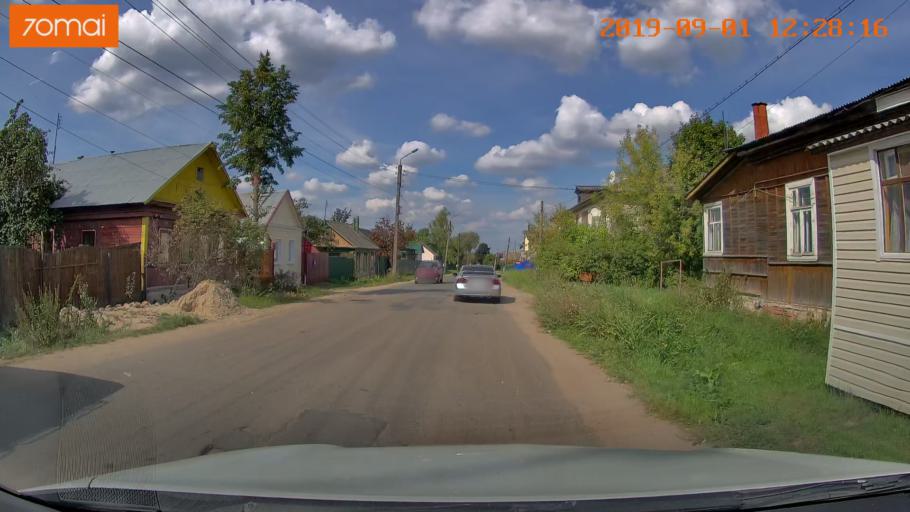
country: RU
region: Kaluga
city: Maloyaroslavets
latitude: 55.0057
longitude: 36.4544
